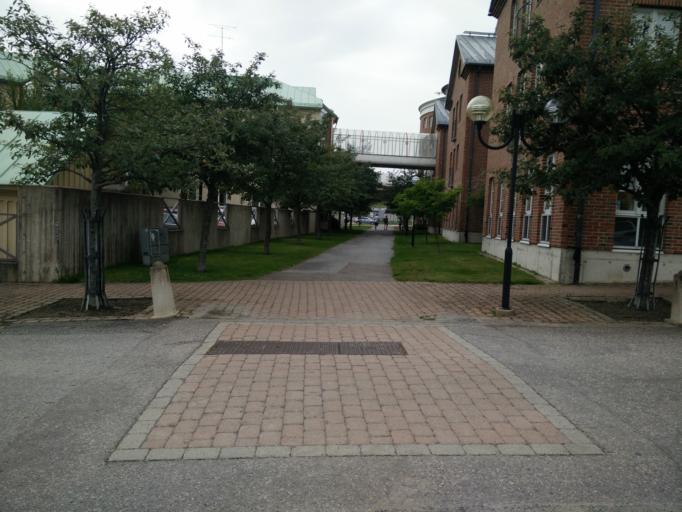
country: SE
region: Vaesternorrland
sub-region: Haernoesands Kommun
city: Haernoesand
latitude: 62.6334
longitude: 17.9294
